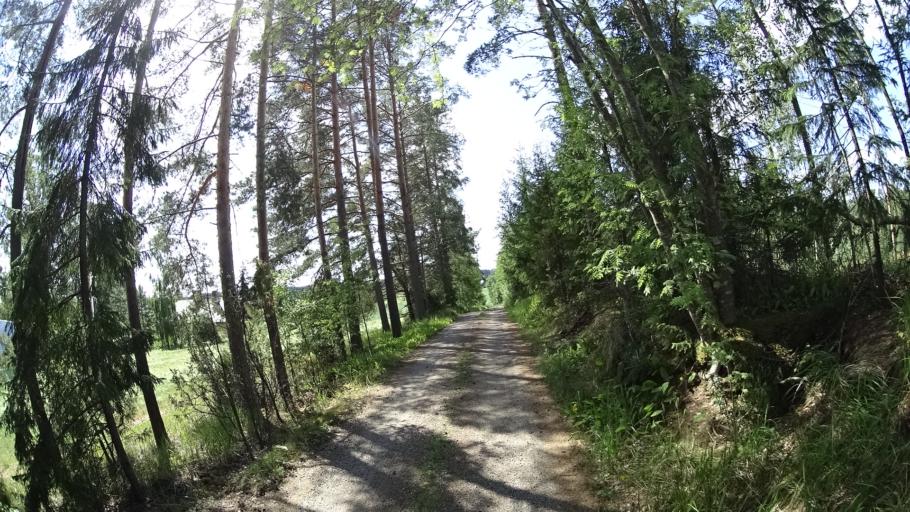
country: FI
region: Haeme
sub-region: Forssa
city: Tammela
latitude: 60.7643
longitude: 23.8877
